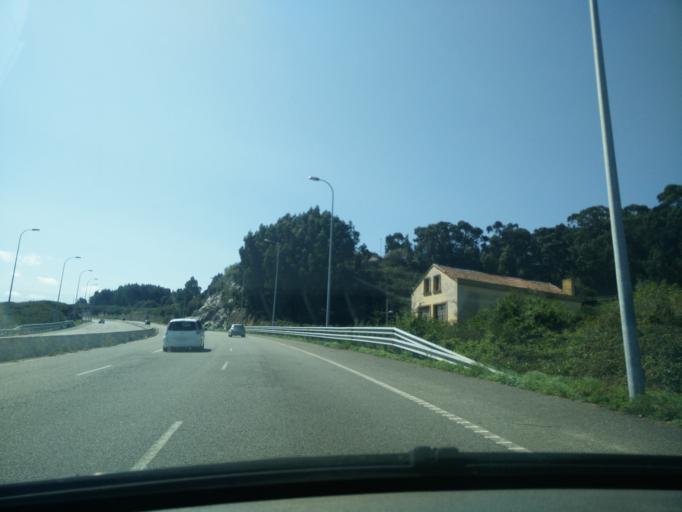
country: ES
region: Galicia
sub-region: Provincia da Coruna
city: A Coruna
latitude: 43.3655
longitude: -8.4317
